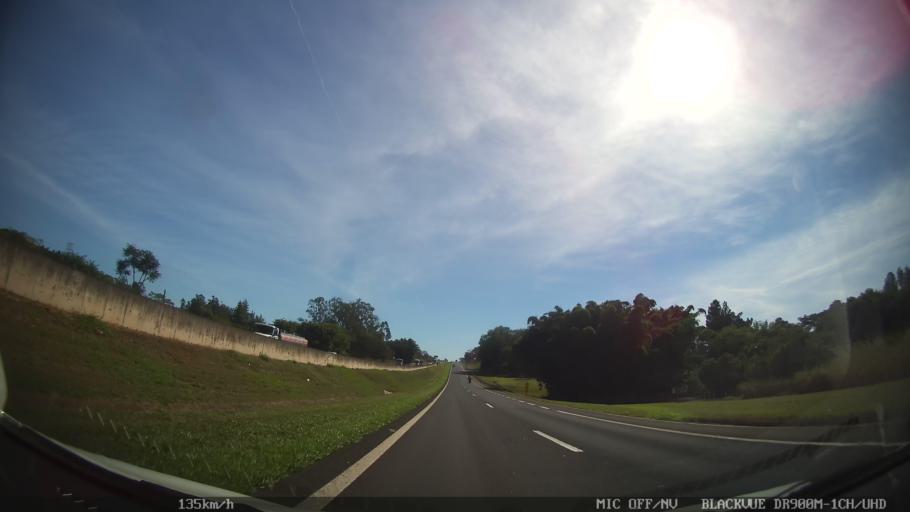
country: BR
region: Sao Paulo
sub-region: Pirassununga
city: Pirassununga
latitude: -21.9947
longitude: -47.4469
